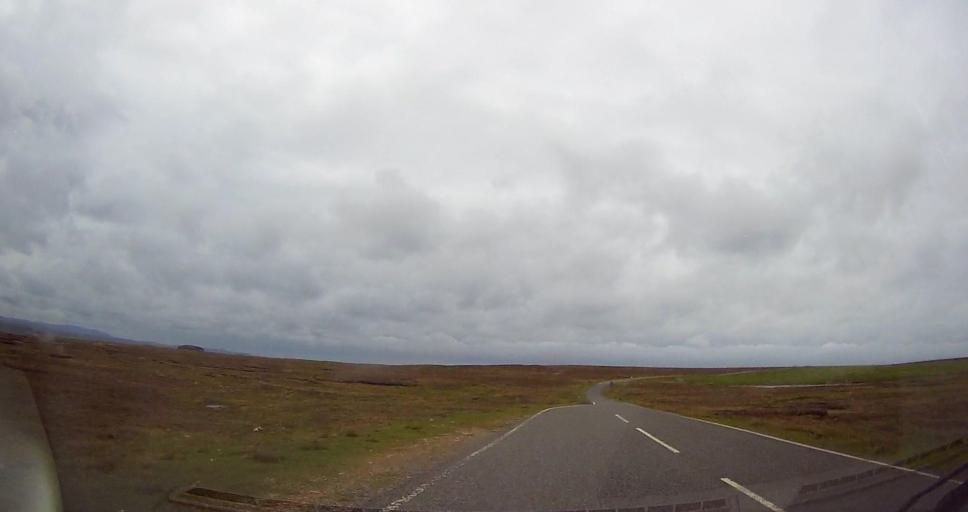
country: GB
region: Scotland
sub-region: Shetland Islands
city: Lerwick
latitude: 60.4903
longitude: -1.5852
